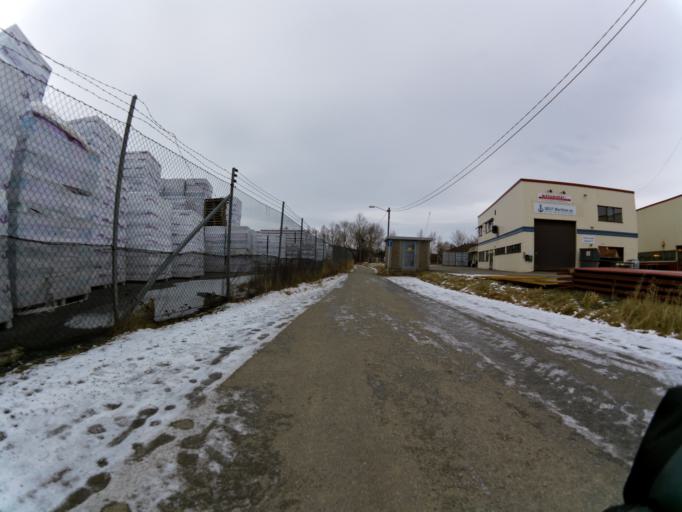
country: NO
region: Ostfold
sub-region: Fredrikstad
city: Fredrikstad
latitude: 59.2067
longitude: 10.8913
